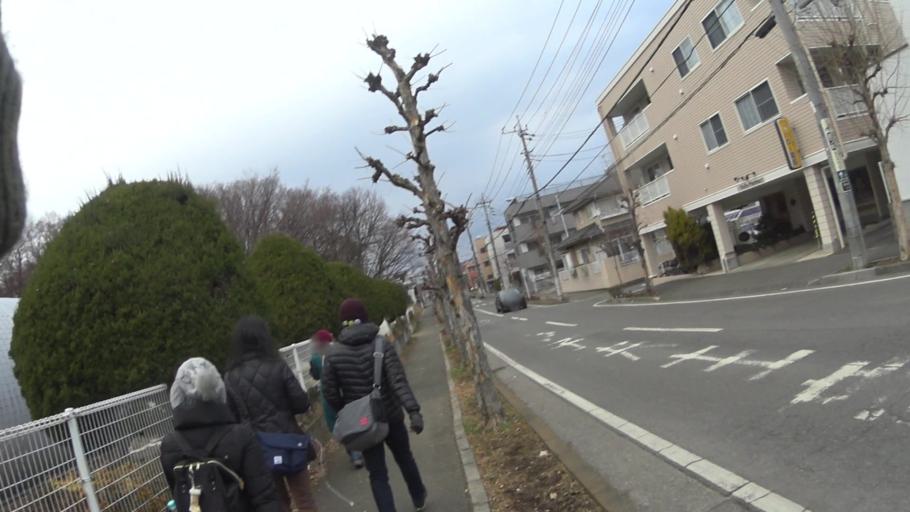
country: JP
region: Saitama
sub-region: Kawaguchi-shi
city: Hatogaya-honcho
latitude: 35.8654
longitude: 139.7024
